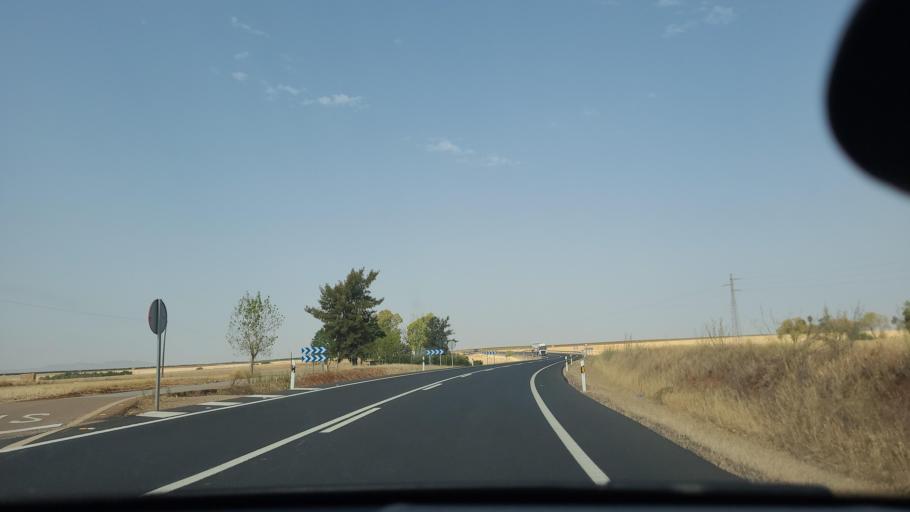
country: ES
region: Extremadura
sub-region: Provincia de Badajoz
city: Berlanga
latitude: 38.2657
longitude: -5.7606
